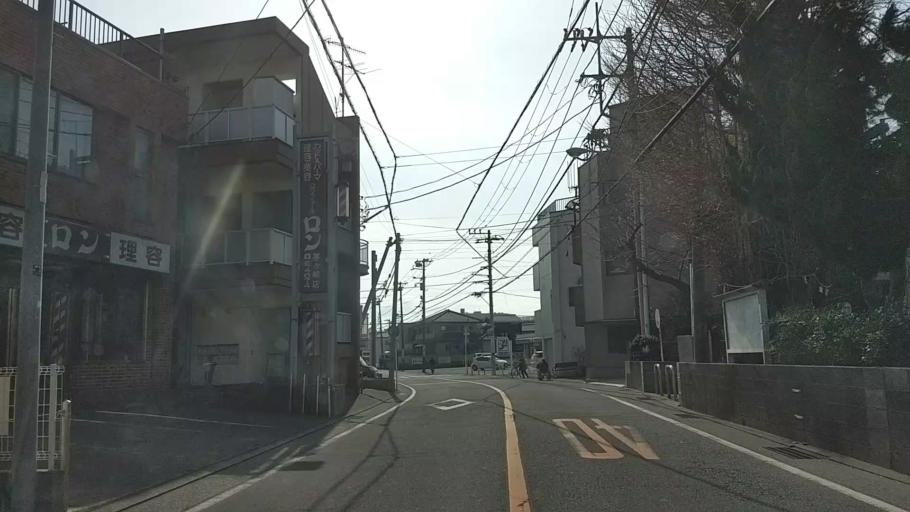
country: JP
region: Kanagawa
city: Chigasaki
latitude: 35.3349
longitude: 139.3825
